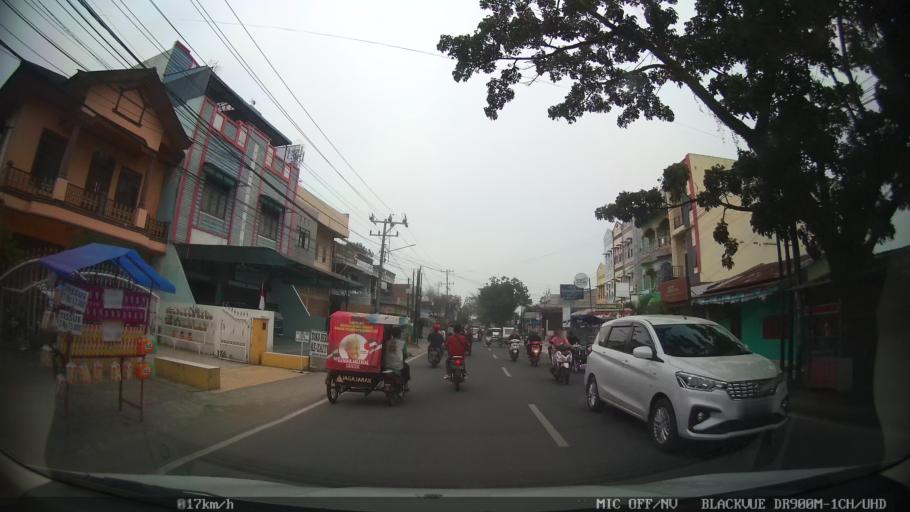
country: ID
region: North Sumatra
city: Medan
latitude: 3.5681
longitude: 98.7216
